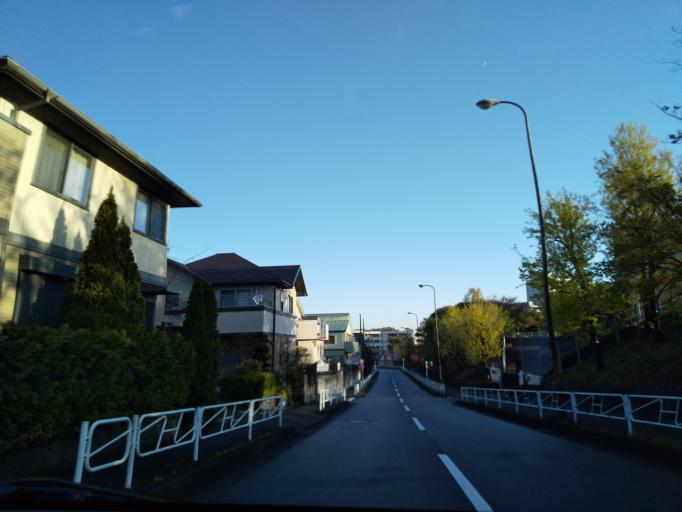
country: JP
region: Tokyo
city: Hachioji
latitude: 35.6153
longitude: 139.3679
